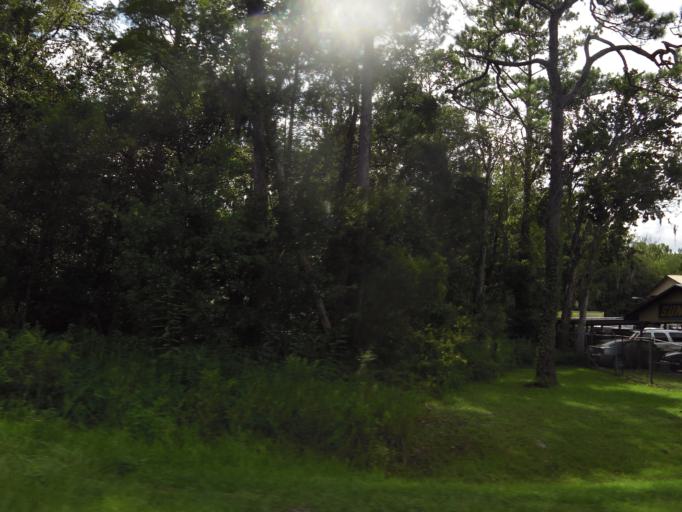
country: US
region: Florida
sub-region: Clay County
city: Green Cove Springs
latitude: 29.9660
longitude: -81.6934
